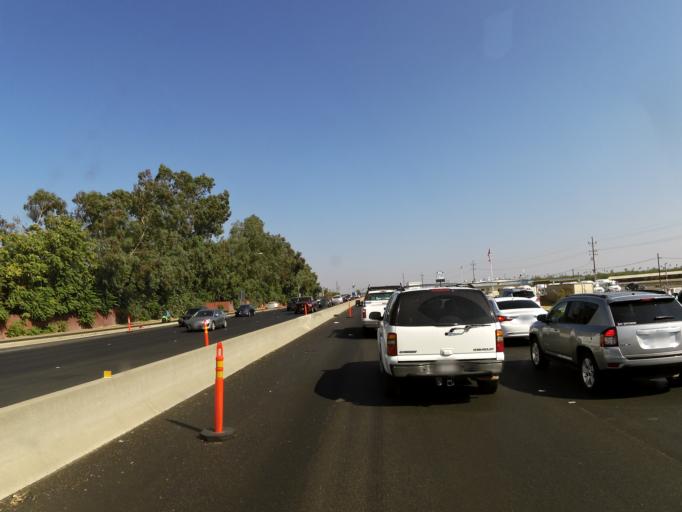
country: US
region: California
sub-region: San Joaquin County
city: Manteca
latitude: 37.7742
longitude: -121.1787
